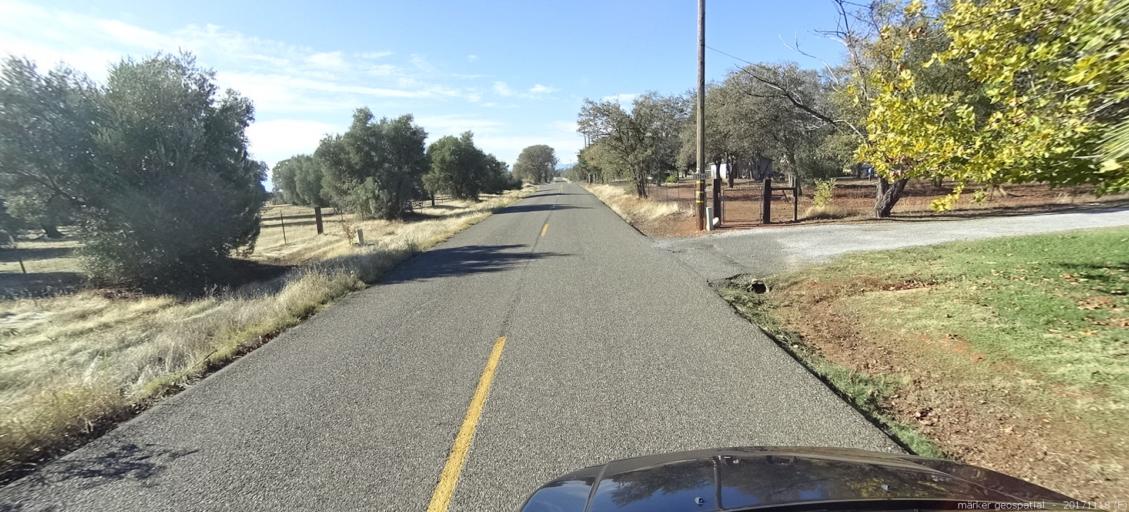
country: US
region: California
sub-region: Shasta County
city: Anderson
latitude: 40.4393
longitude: -122.4250
